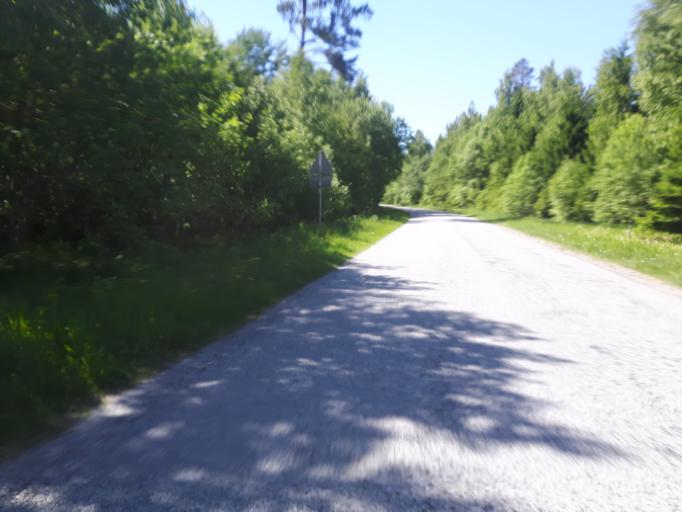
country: EE
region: Laeaene-Virumaa
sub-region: Haljala vald
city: Haljala
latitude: 59.5517
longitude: 26.3658
